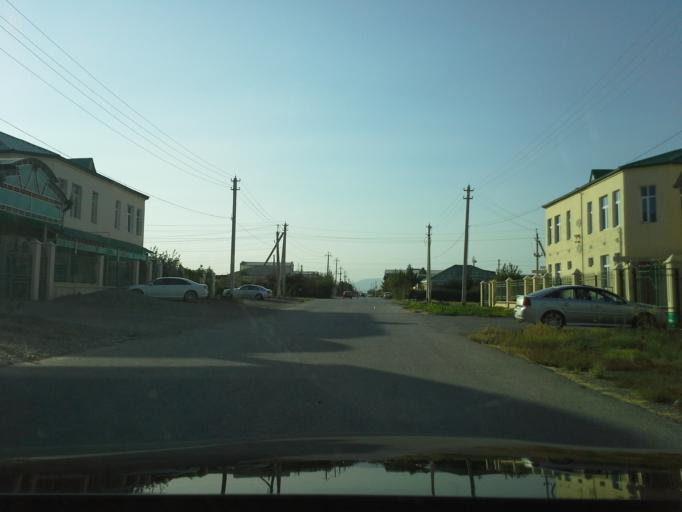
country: TM
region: Ahal
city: Abadan
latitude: 38.0482
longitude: 58.1704
